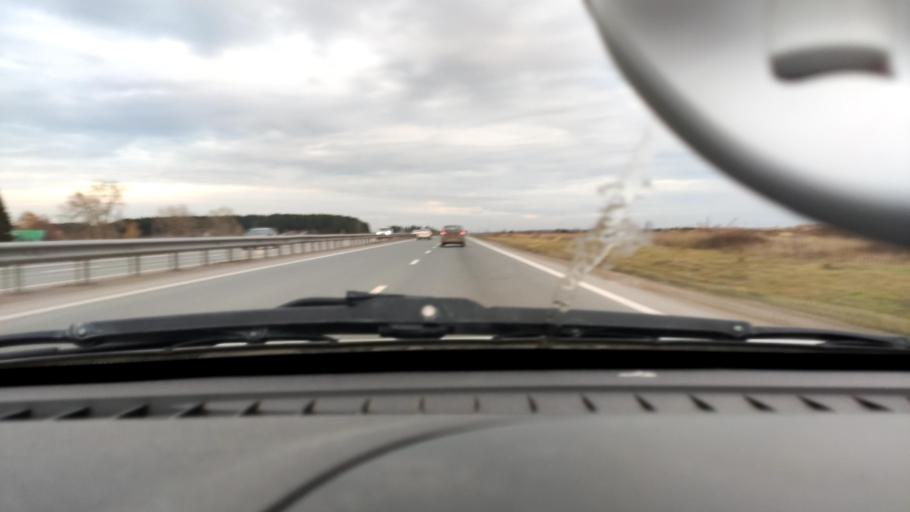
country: RU
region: Perm
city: Froly
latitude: 57.9339
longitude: 56.2440
